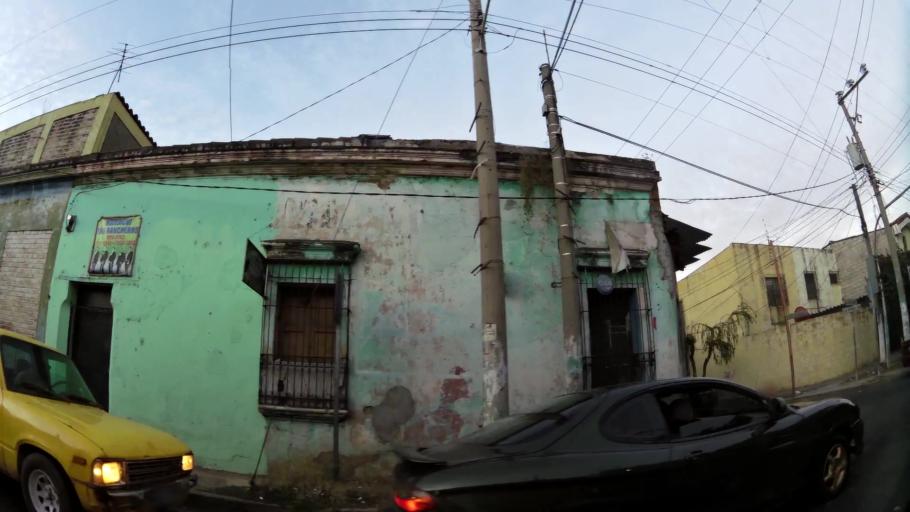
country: SV
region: Santa Ana
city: Santa Ana
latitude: 13.9893
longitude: -89.5568
